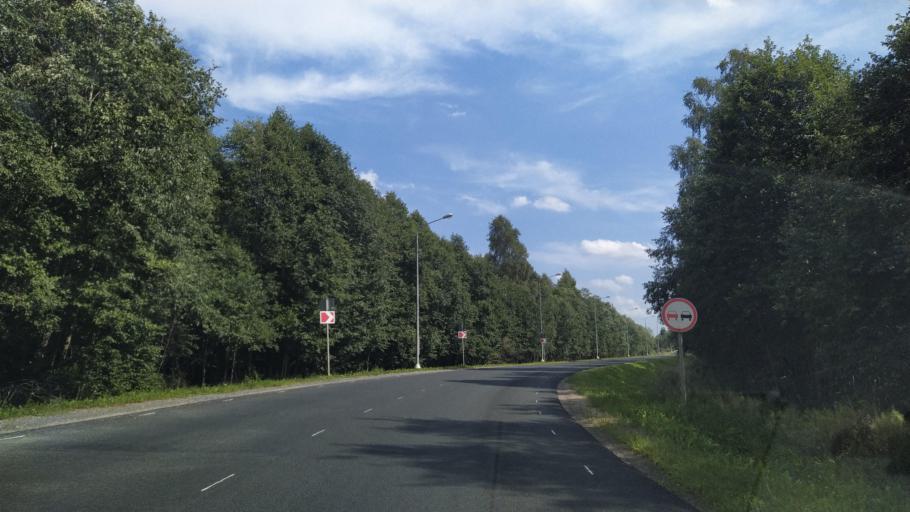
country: RU
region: Pskov
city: Porkhov
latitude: 57.7437
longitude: 29.0467
